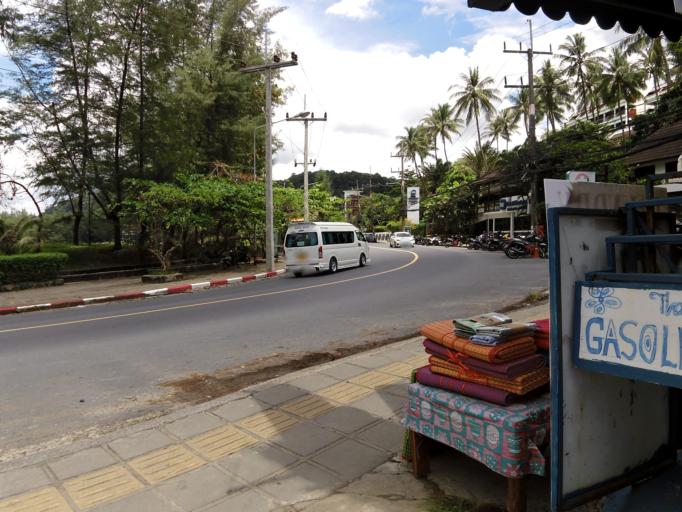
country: TH
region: Phuket
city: Ban Karon
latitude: 7.8512
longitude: 98.2950
